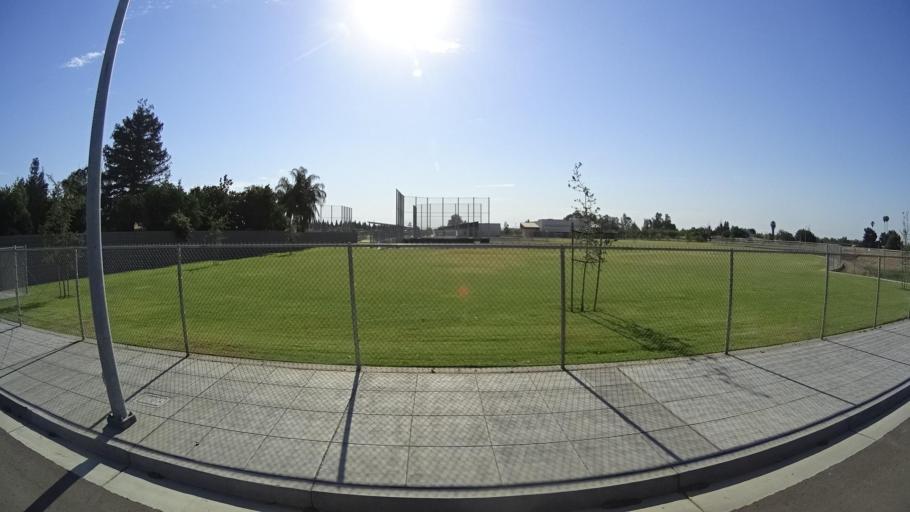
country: US
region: California
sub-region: Fresno County
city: Tarpey Village
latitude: 36.7823
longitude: -119.6551
